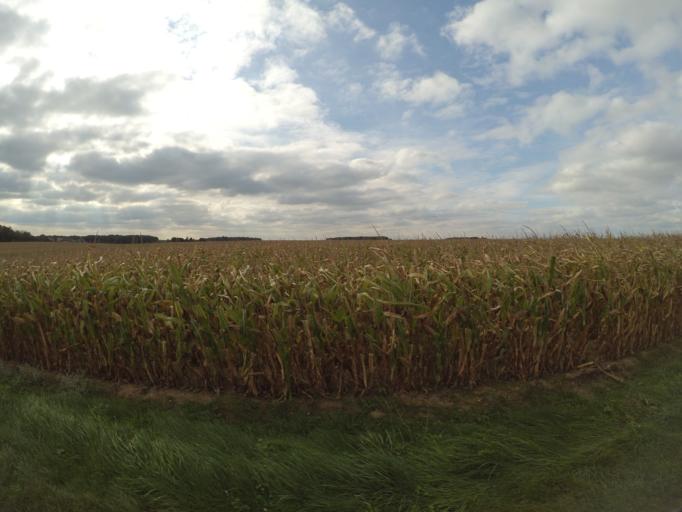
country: FR
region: Centre
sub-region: Departement d'Indre-et-Loire
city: Nazelles-Negron
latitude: 47.4739
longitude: 0.9429
